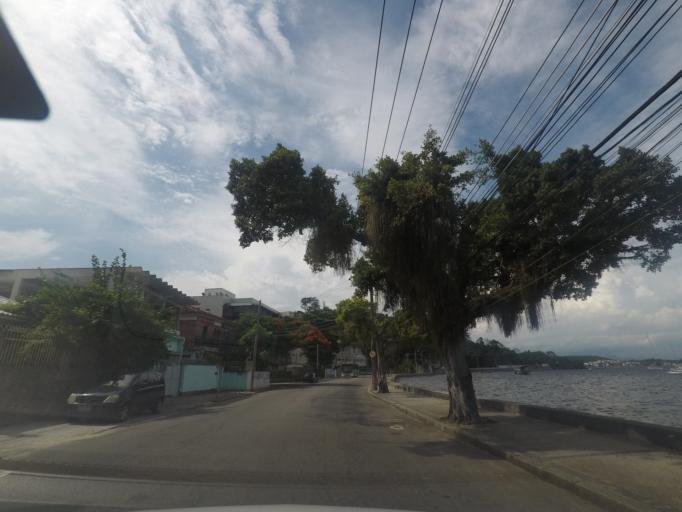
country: BR
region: Rio de Janeiro
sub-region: Rio De Janeiro
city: Rio de Janeiro
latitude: -22.8165
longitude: -43.1764
